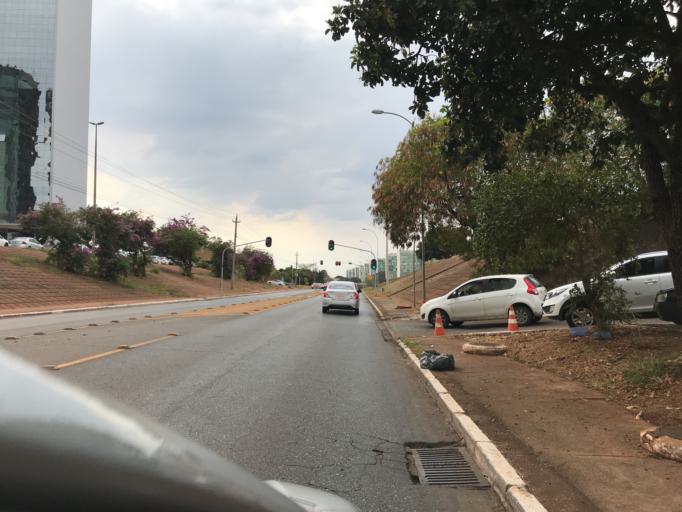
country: BR
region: Federal District
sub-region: Brasilia
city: Brasilia
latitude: -15.7914
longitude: -47.8796
